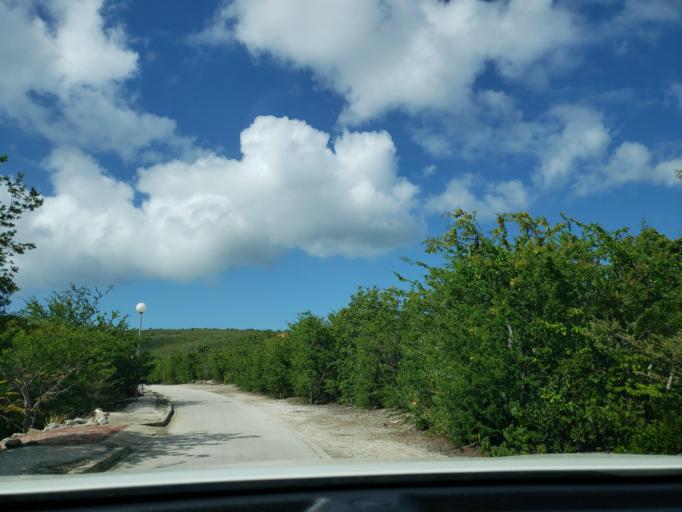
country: CW
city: Dorp Soto
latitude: 12.2021
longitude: -69.0783
